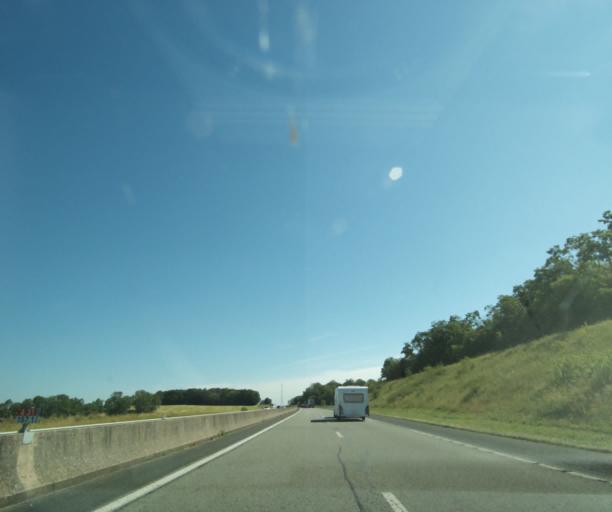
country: FR
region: Lorraine
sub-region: Departement des Vosges
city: Lamarche
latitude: 48.1086
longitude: 5.6551
